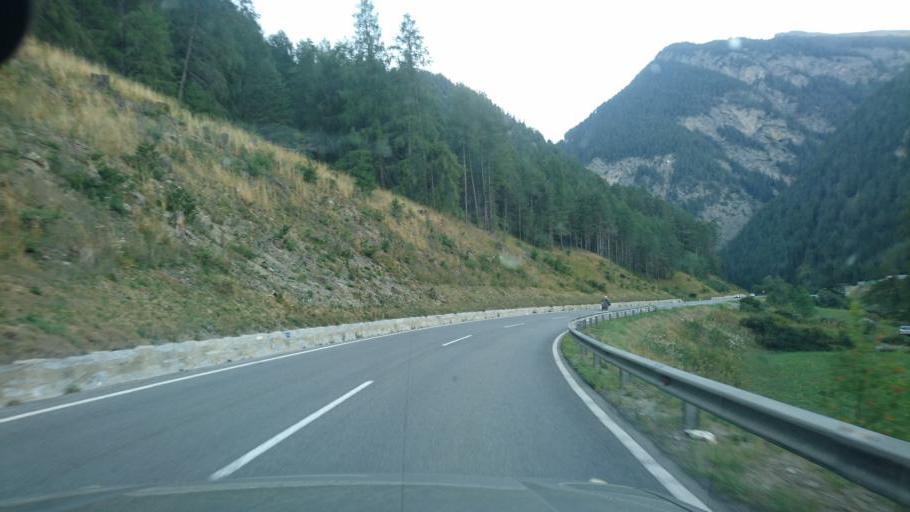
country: AT
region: Tyrol
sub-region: Politischer Bezirk Landeck
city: Nauders
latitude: 46.9018
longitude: 10.4923
